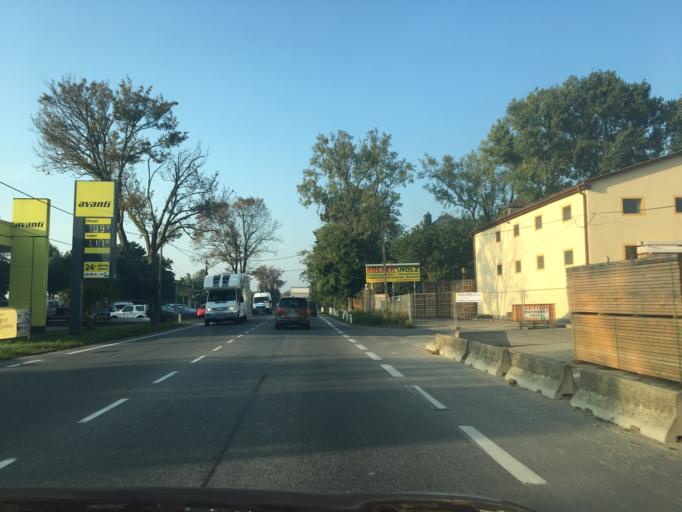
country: AT
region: Lower Austria
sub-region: Politischer Bezirk Korneuburg
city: Hagenbrunn
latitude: 48.3119
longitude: 16.4301
